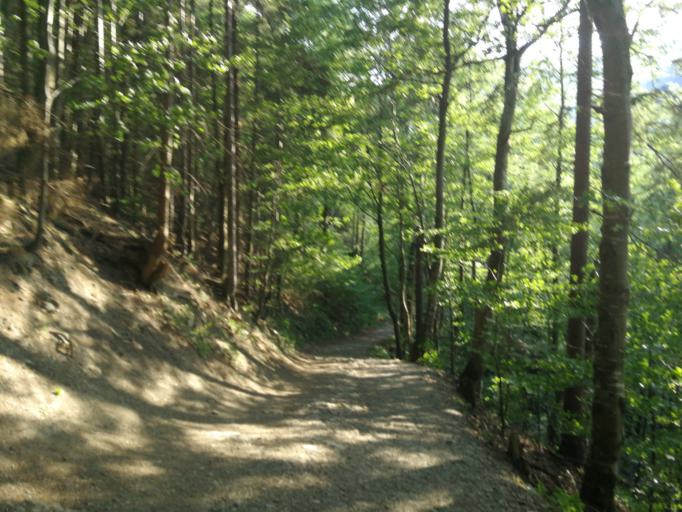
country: SK
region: Zilinsky
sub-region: Okres Liptovsky Mikulas
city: Liptovsky Mikulas
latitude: 49.1883
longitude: 19.5458
